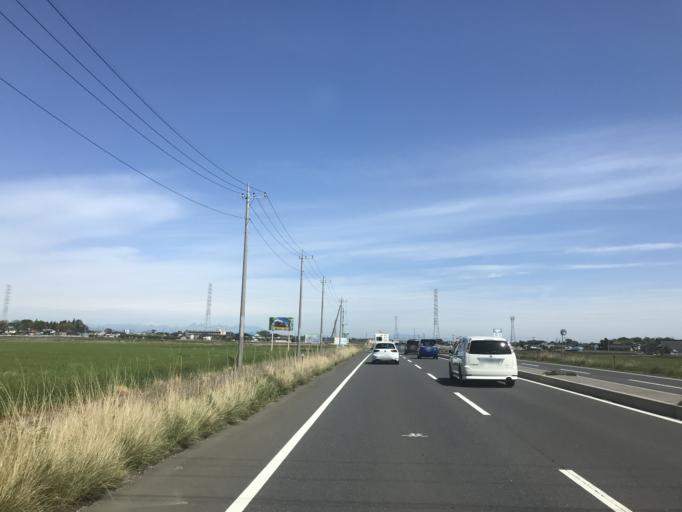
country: JP
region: Ibaraki
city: Ishige
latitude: 36.1672
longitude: 139.9936
